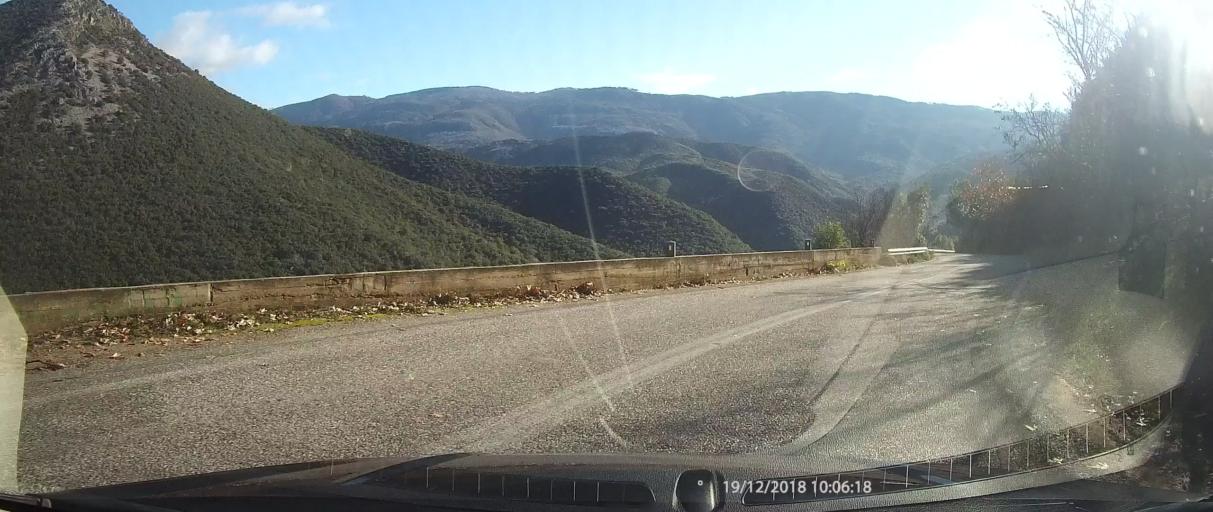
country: GR
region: Peloponnese
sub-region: Nomos Messinias
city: Paralia Vergas
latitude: 37.1138
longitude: 22.2097
